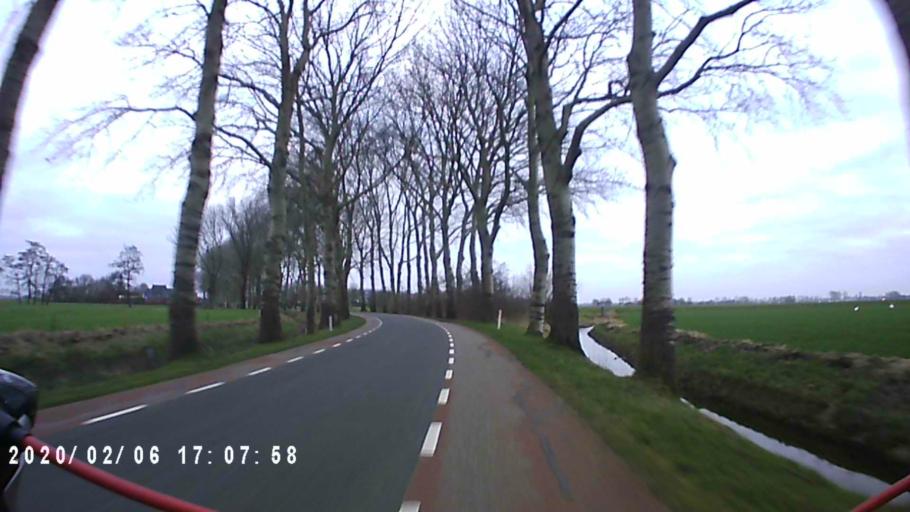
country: NL
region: Groningen
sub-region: Gemeente Winsum
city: Winsum
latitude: 53.2751
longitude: 6.5238
